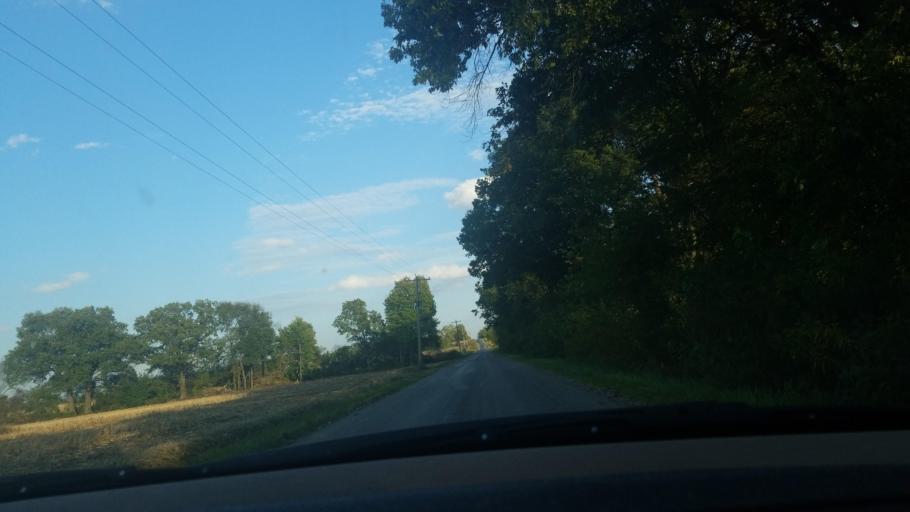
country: US
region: Illinois
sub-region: Saline County
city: Carrier Mills
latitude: 37.8050
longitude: -88.6720
